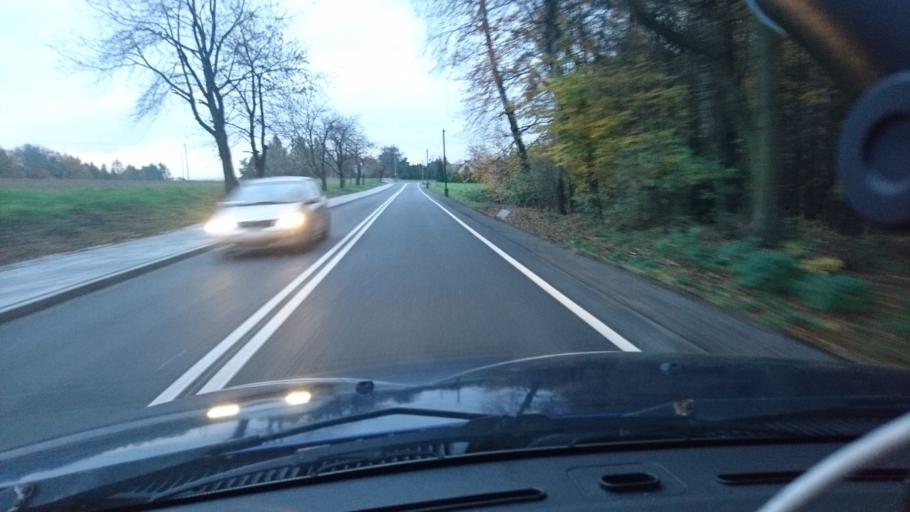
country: PL
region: Silesian Voivodeship
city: Janowice
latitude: 49.9062
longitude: 19.0852
